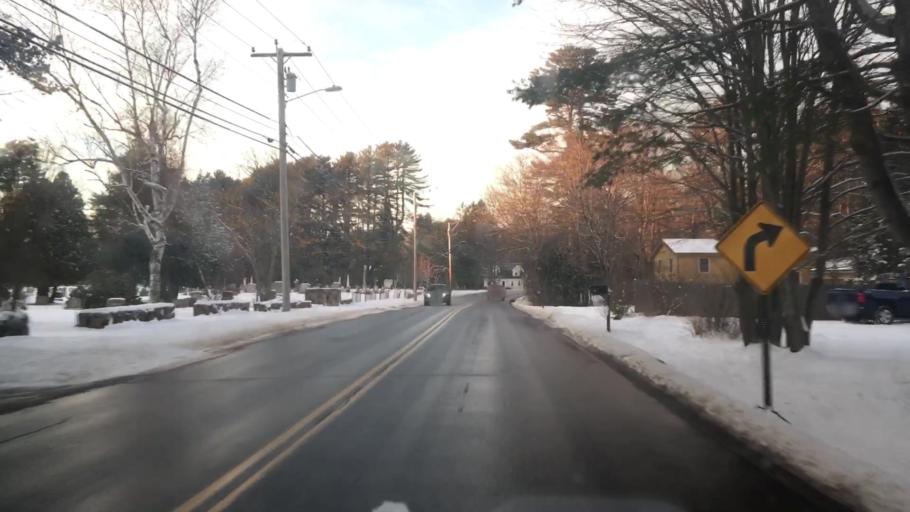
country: US
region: Maine
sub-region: Cumberland County
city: Brunswick
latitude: 43.9502
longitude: -69.9297
